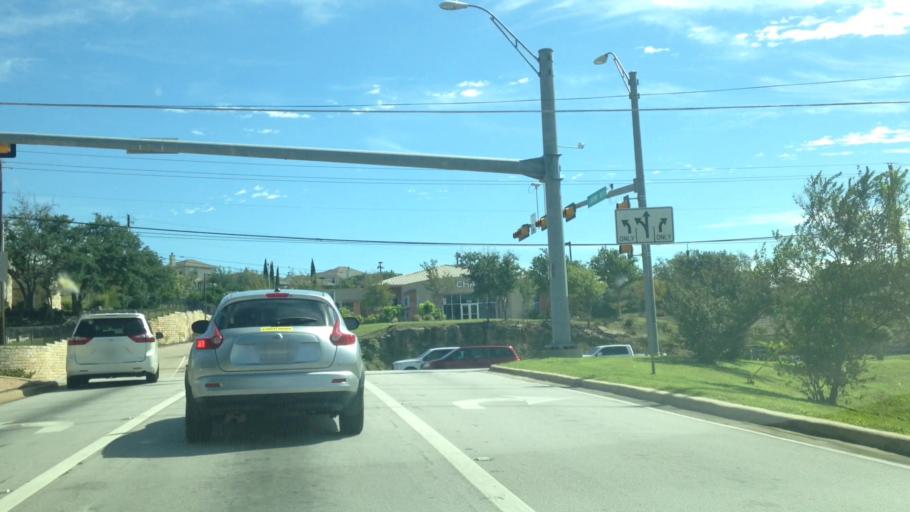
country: US
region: Texas
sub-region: Travis County
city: Lakeway
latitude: 30.3543
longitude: -97.9620
